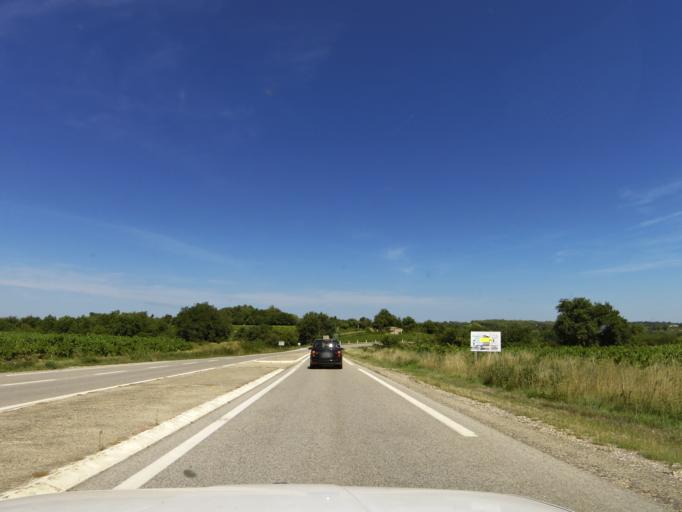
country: FR
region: Languedoc-Roussillon
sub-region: Departement du Gard
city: Sabran
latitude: 44.1357
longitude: 4.4748
